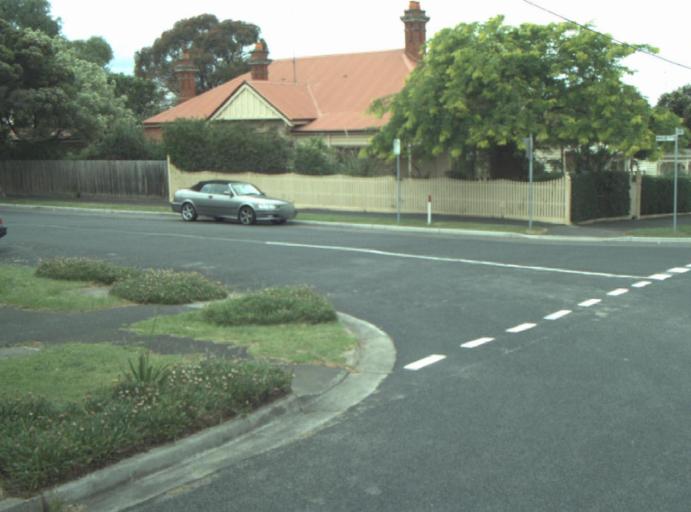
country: AU
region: Victoria
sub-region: Greater Geelong
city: Geelong
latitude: -38.1550
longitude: 144.3601
